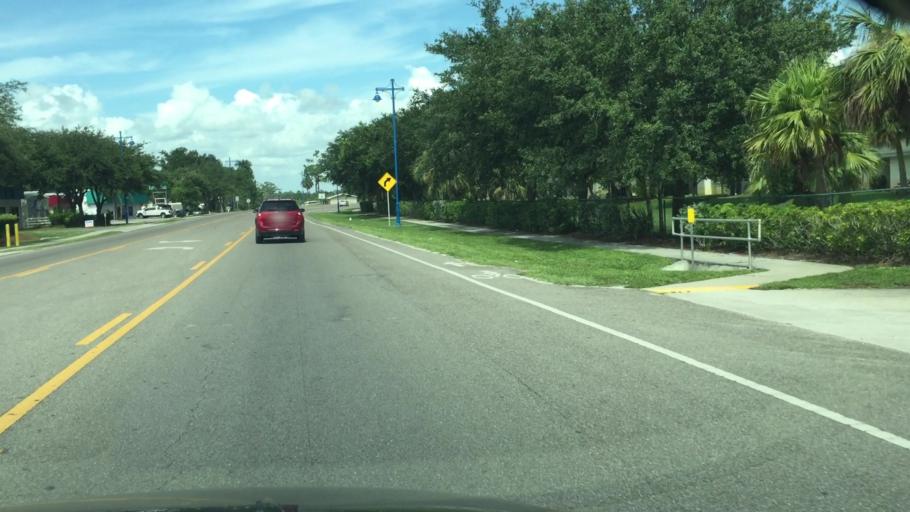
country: US
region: Florida
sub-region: Collier County
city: Immokalee
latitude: 26.4186
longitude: -81.4277
